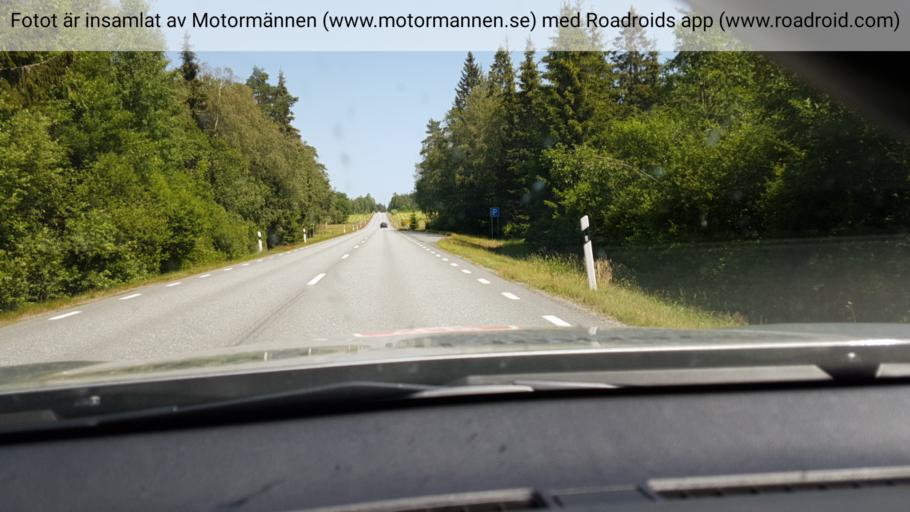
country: SE
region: Joenkoeping
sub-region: Nassjo Kommun
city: Bodafors
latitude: 57.4470
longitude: 14.7172
